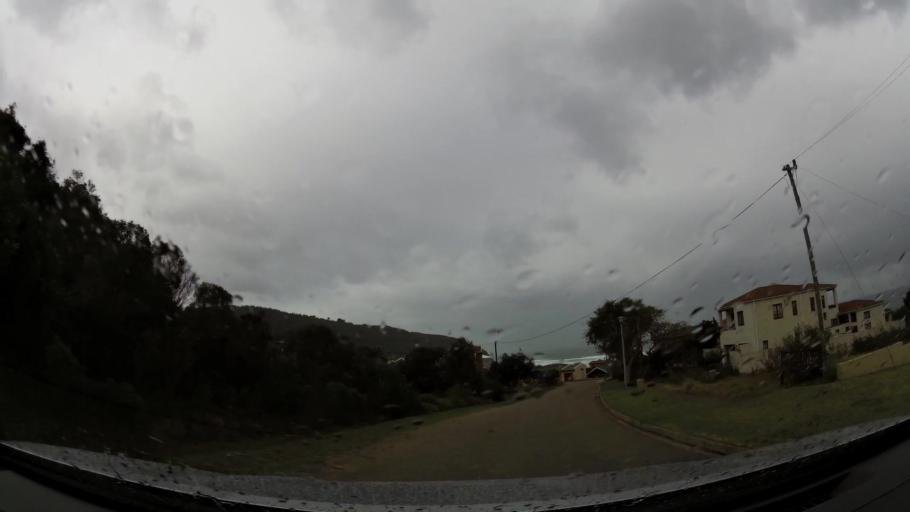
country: ZA
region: Western Cape
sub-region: Eden District Municipality
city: George
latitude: -34.0479
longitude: 22.3100
